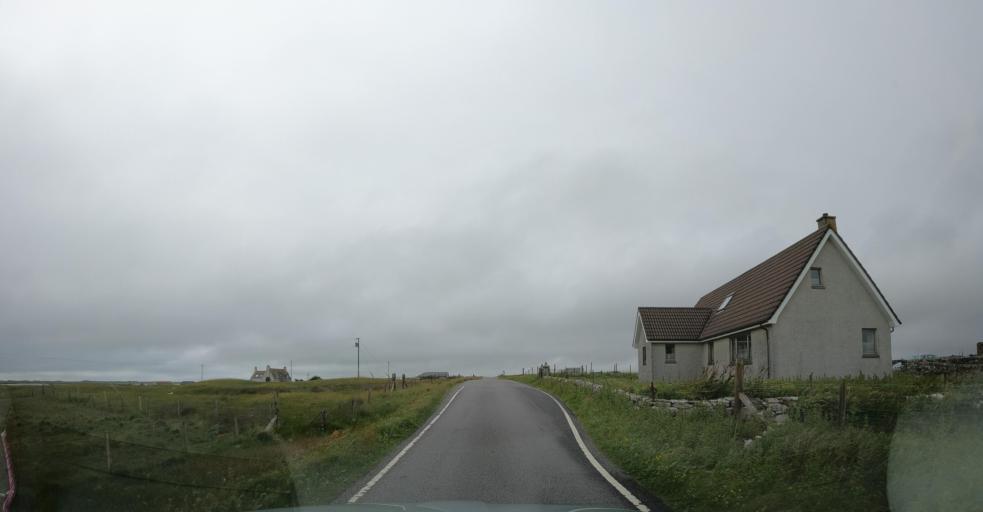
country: GB
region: Scotland
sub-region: Eilean Siar
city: Isle of North Uist
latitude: 57.5665
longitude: -7.3861
